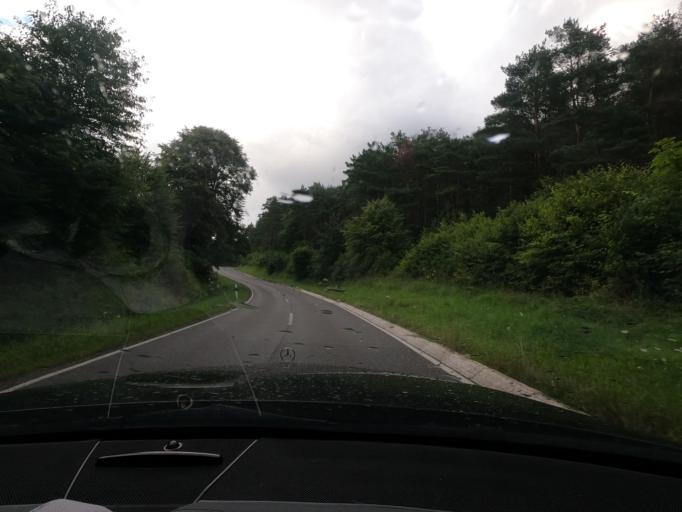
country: DE
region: Hesse
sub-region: Regierungsbezirk Kassel
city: Wolfhagen
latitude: 51.3193
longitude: 9.1929
